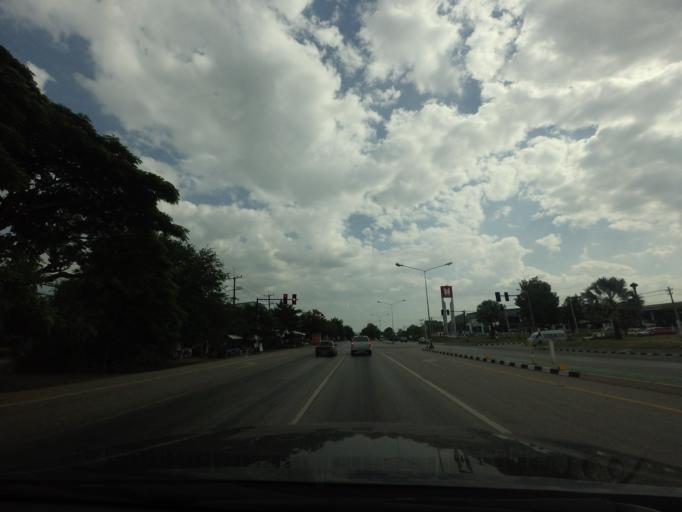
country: TH
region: Lop Buri
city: Chai Badan
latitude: 15.2338
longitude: 101.1267
